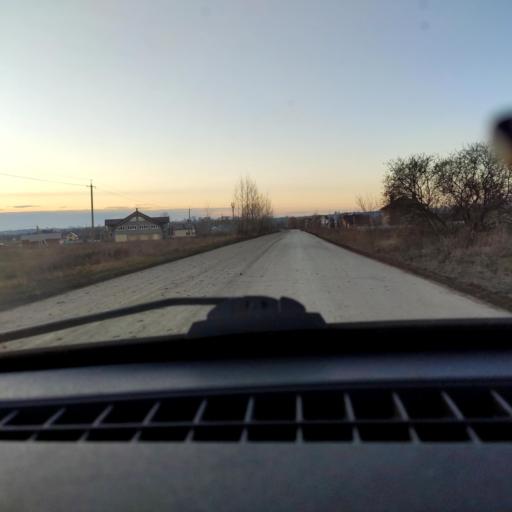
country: RU
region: Bashkortostan
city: Ufa
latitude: 54.7049
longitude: 56.1126
